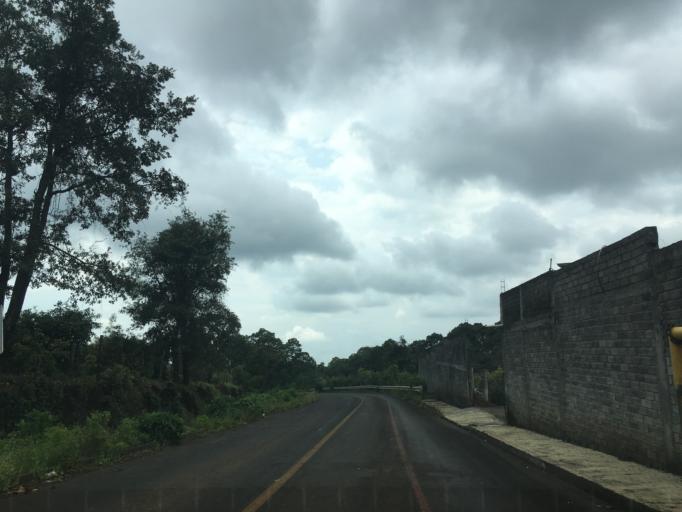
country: MX
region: Michoacan
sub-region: Los Reyes
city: Atapan
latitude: 19.6095
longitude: -102.3993
